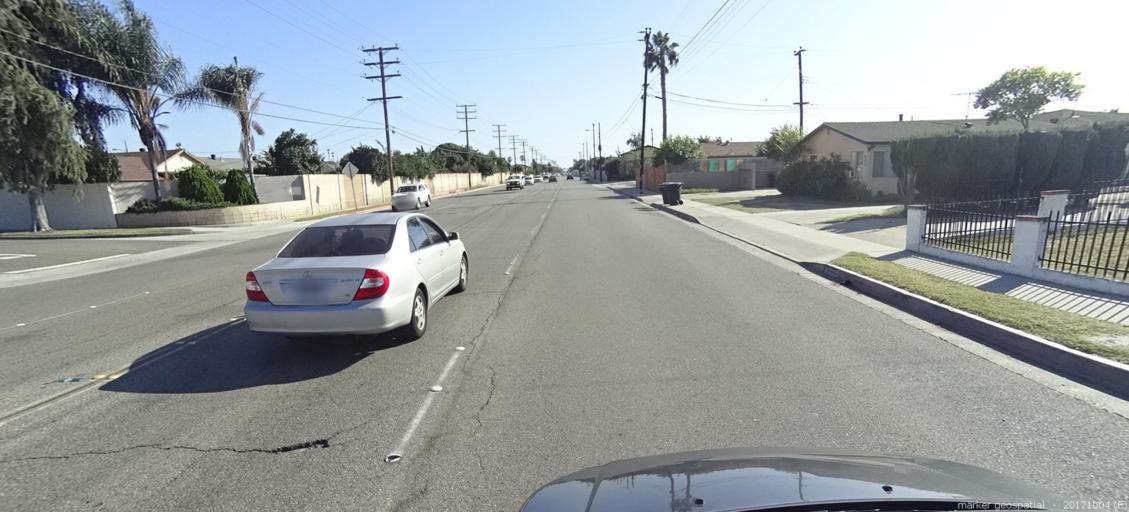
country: US
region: California
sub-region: Orange County
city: Midway City
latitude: 33.7655
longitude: -117.9812
